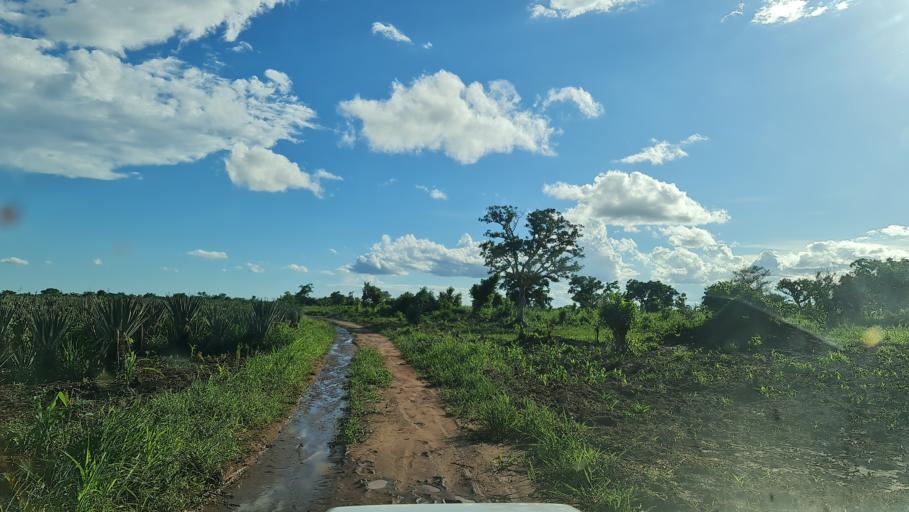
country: MZ
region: Nampula
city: Ilha de Mocambique
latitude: -14.9390
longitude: 40.2009
